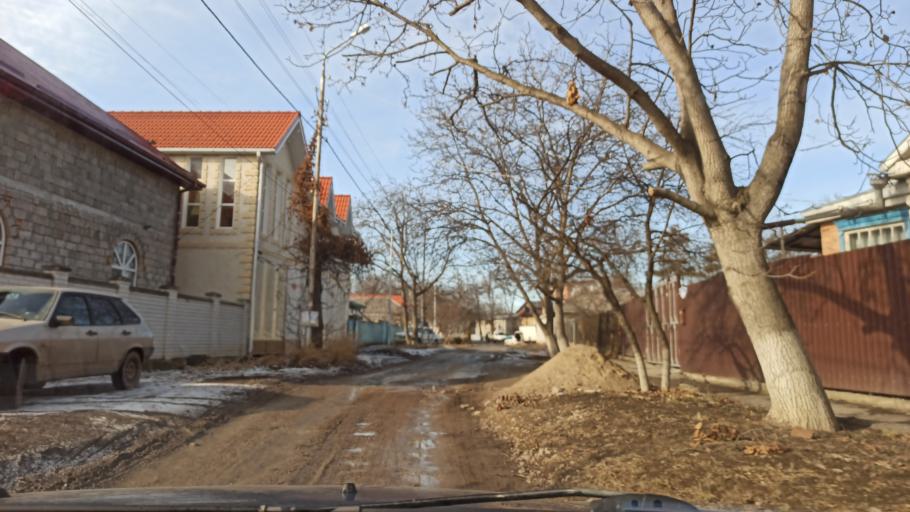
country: RU
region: Stavropol'skiy
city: Yessentukskaya
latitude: 44.0410
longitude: 42.8816
